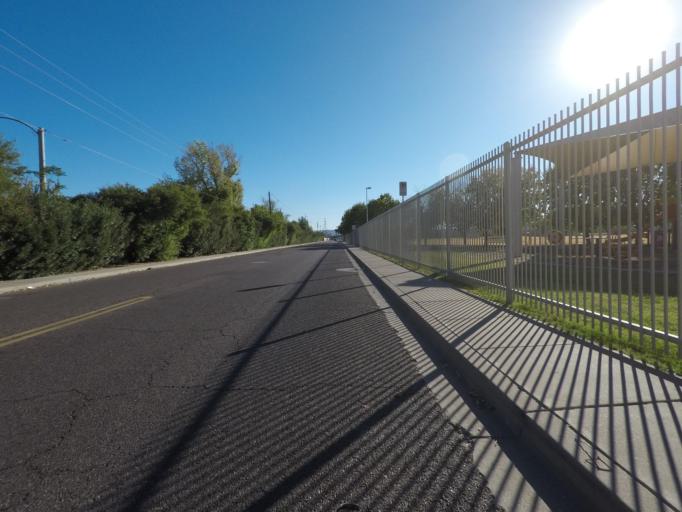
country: US
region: Arizona
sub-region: Maricopa County
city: Phoenix
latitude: 33.4767
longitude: -112.1086
